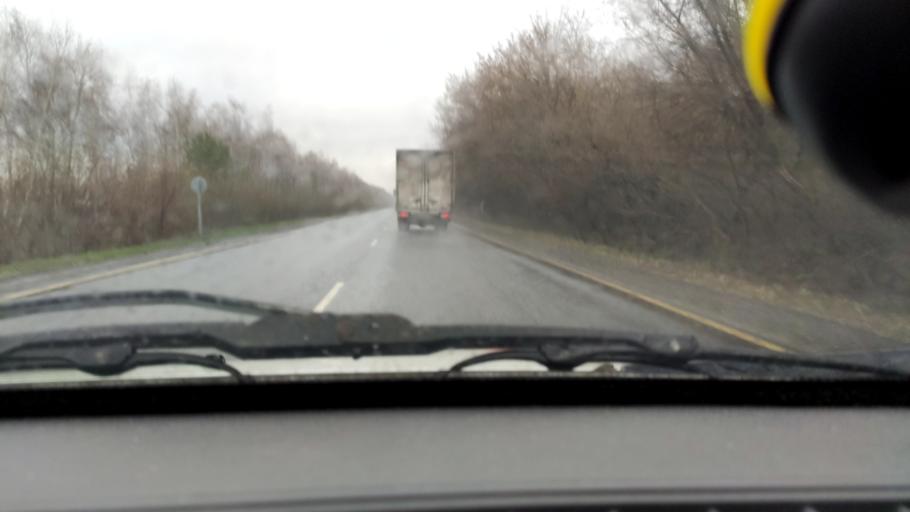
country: RU
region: Samara
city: Povolzhskiy
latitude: 53.6057
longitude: 49.6061
